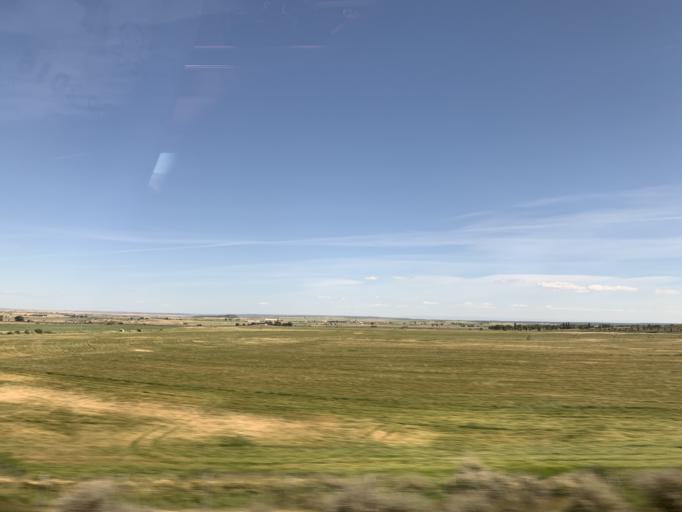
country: ES
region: Aragon
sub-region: Provincia de Huesca
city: Candasnos
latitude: 41.5325
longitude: 0.0416
